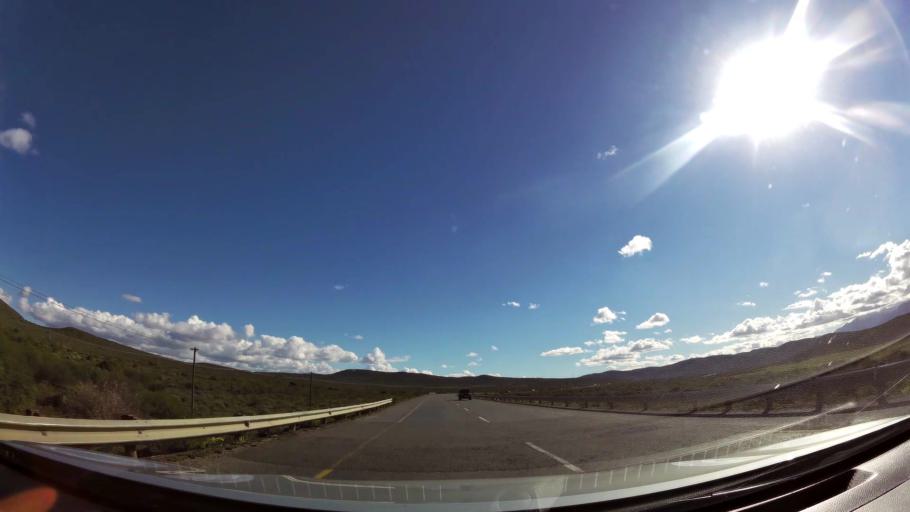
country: ZA
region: Western Cape
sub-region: Cape Winelands District Municipality
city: Worcester
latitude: -33.7505
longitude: 19.7130
